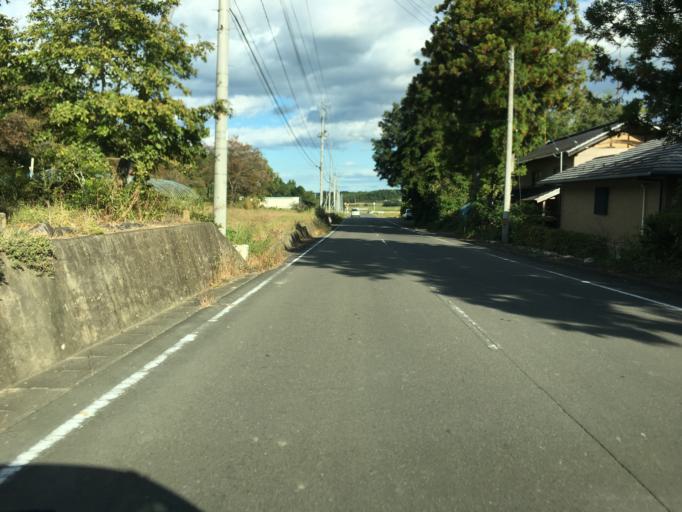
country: JP
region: Miyagi
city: Marumori
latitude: 37.8637
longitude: 140.8944
